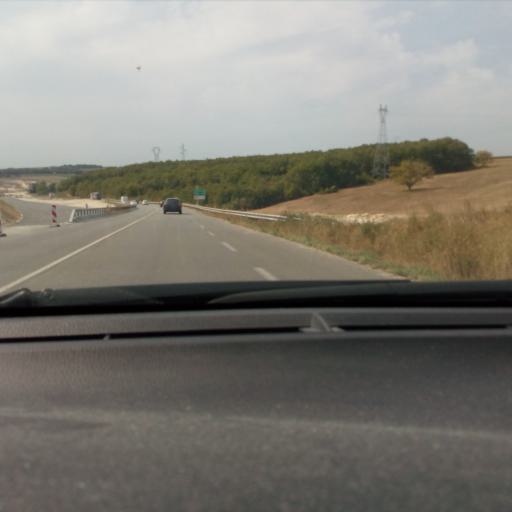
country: FR
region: Poitou-Charentes
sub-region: Departement de la Charente
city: Saint-Saturnin
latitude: 45.6806
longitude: 0.0667
